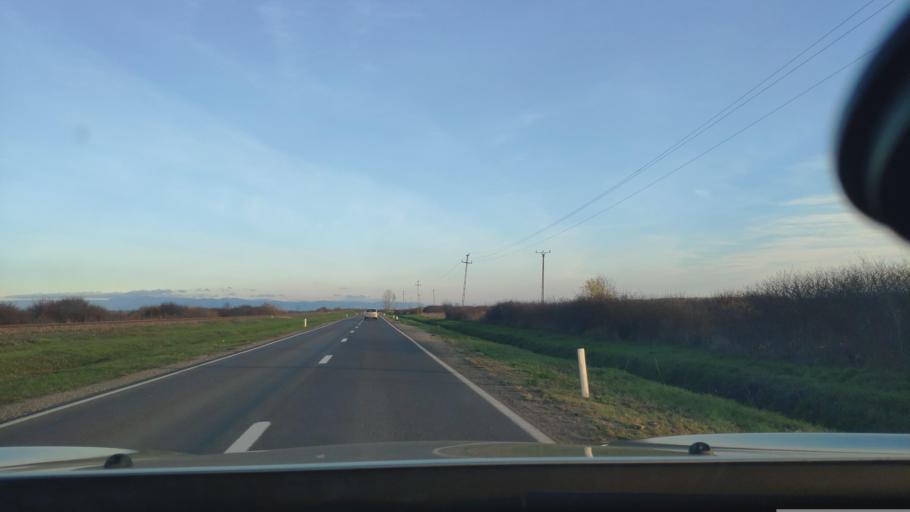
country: RO
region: Satu Mare
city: Culciu Mic
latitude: 47.7894
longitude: 23.0433
